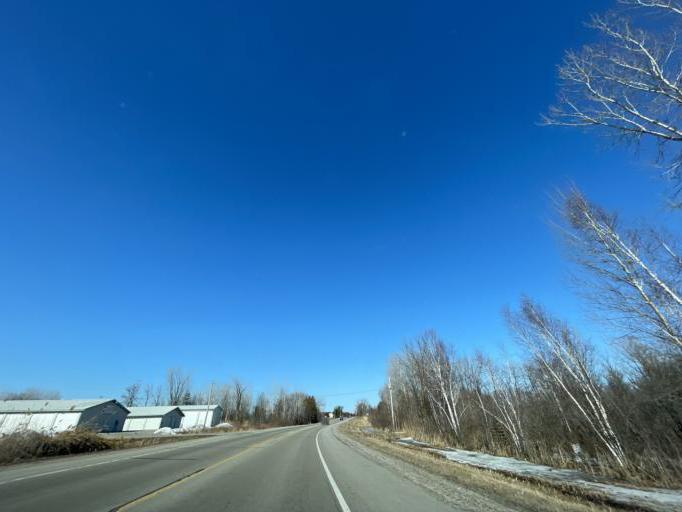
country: US
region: Wisconsin
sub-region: Brown County
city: Suamico
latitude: 44.6025
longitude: -88.0776
